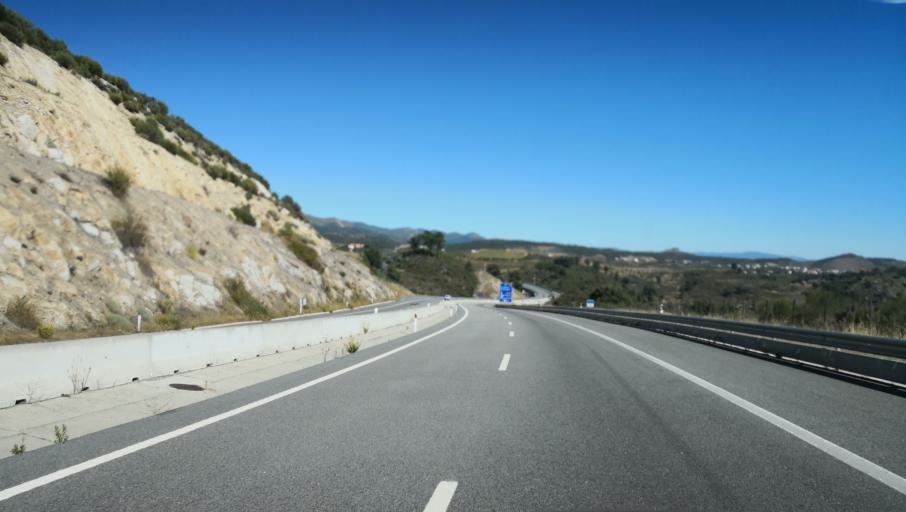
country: PT
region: Vila Real
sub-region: Murca
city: Murca
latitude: 41.3891
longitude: -7.4583
